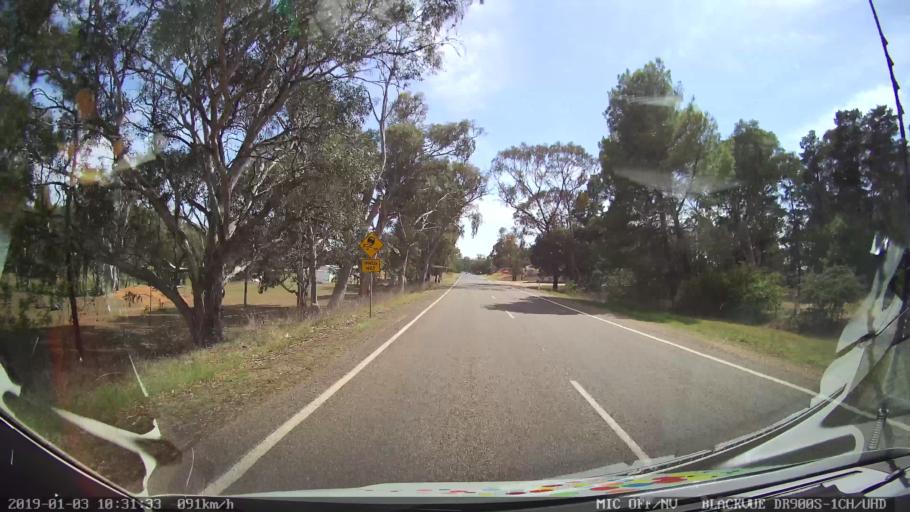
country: AU
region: New South Wales
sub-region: Young
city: Young
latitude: -34.3489
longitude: 148.2784
